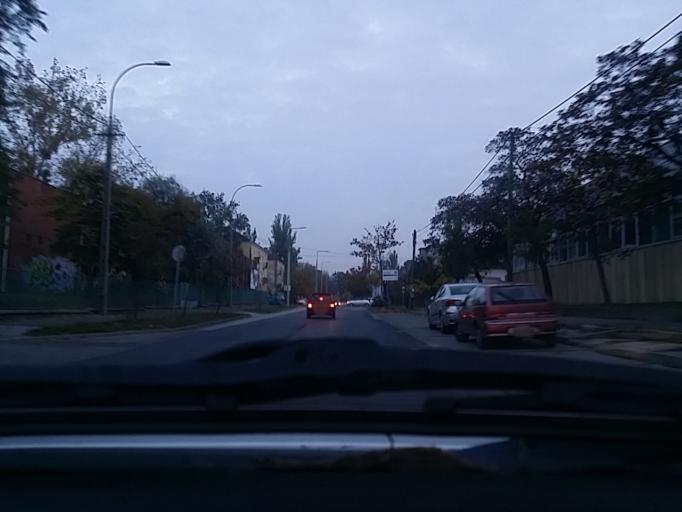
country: HU
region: Budapest
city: Budapest XV. keruelet
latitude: 47.5410
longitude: 19.1190
